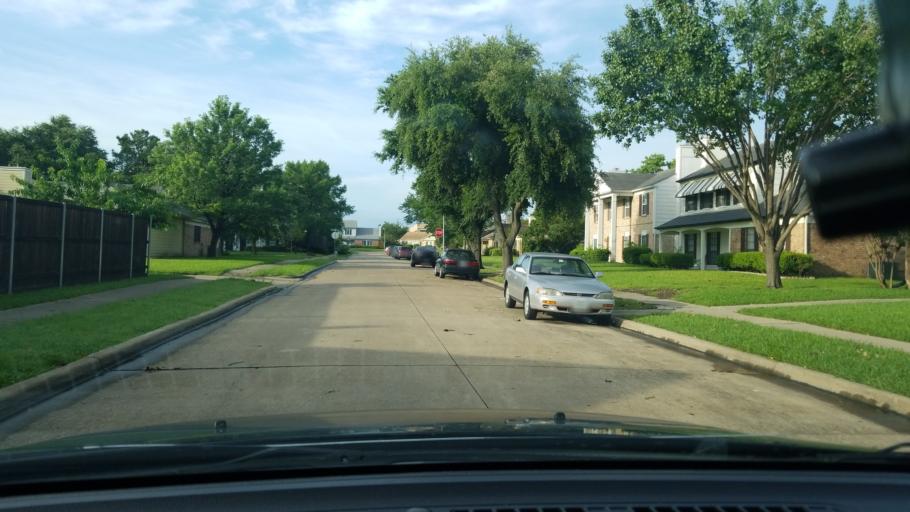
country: US
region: Texas
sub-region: Dallas County
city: Mesquite
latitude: 32.7960
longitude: -96.6019
